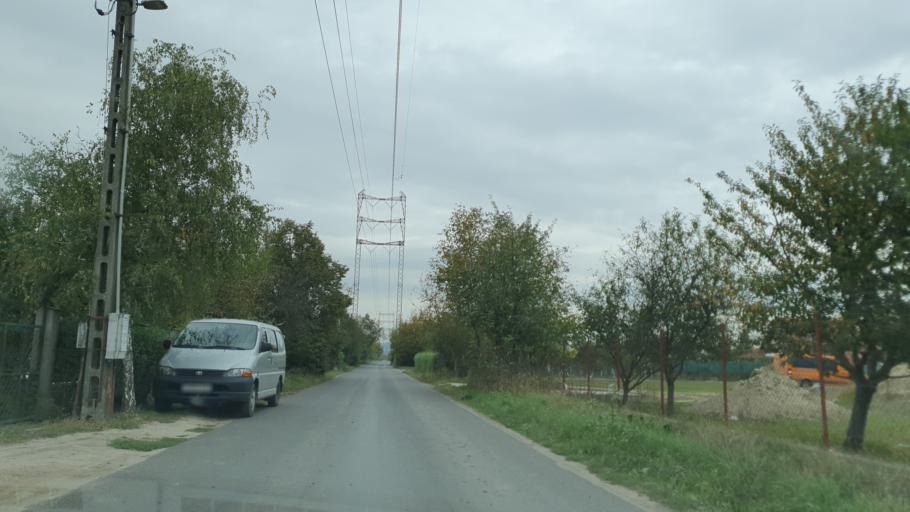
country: HU
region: Pest
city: Dunaharaszti
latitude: 47.3872
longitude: 19.0748
